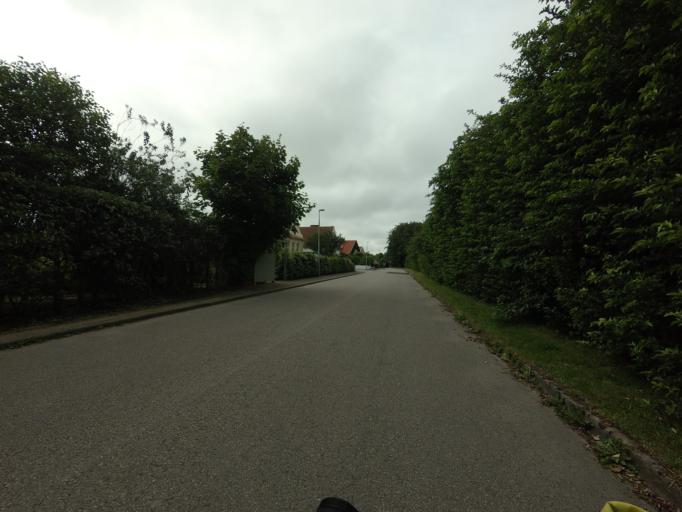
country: SE
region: Skane
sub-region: Hoganas Kommun
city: Hoganas
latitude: 56.1963
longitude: 12.5670
